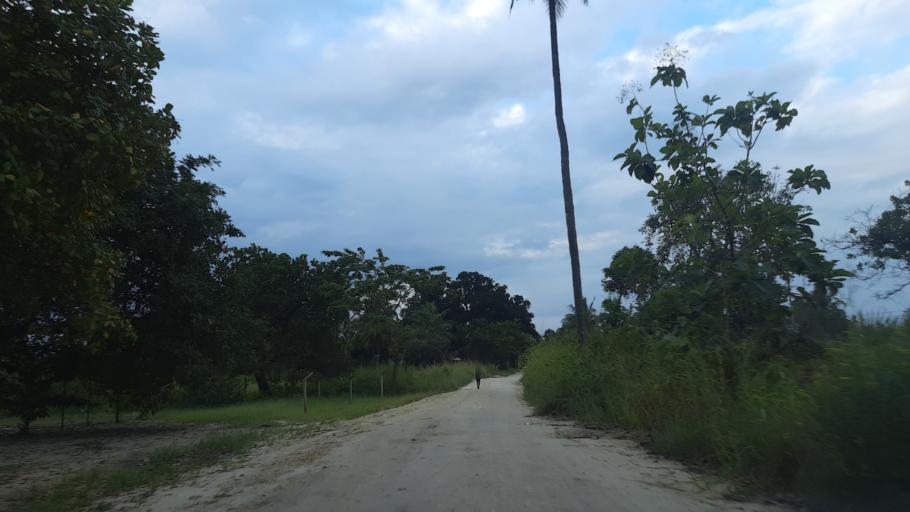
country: TZ
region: Pwani
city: Bagamoyo
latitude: -6.5198
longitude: 38.9266
